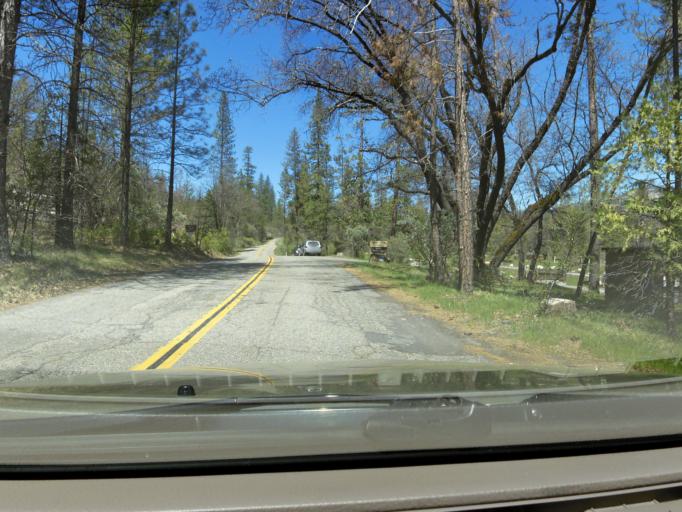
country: US
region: California
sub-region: Madera County
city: Oakhurst
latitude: 37.3243
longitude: -119.5796
